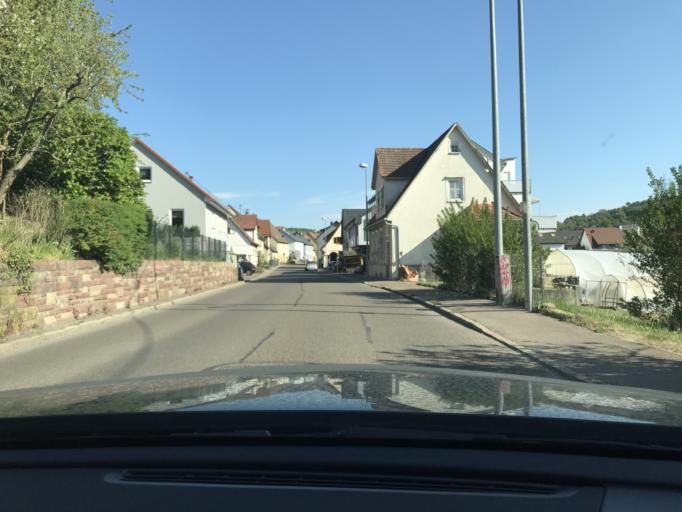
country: DE
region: Baden-Wuerttemberg
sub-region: Regierungsbezirk Stuttgart
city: Weinstadt-Endersbach
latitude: 48.7931
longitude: 9.3997
